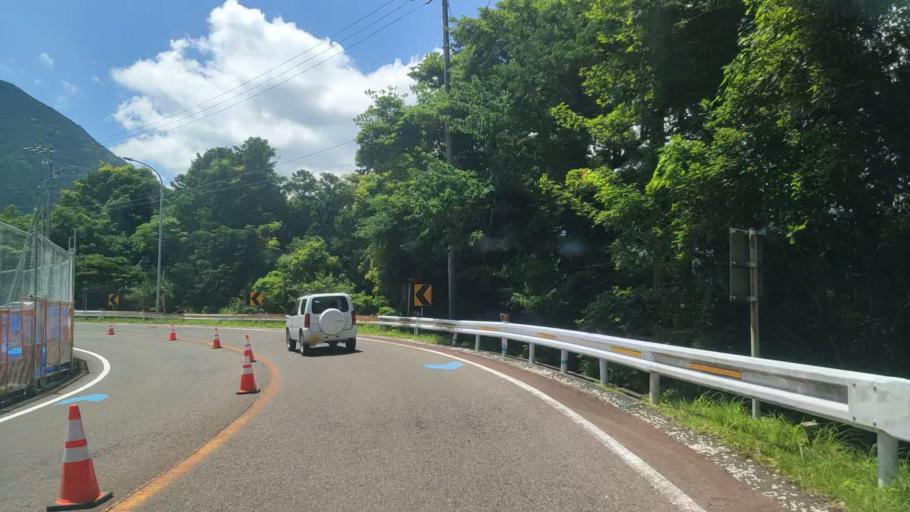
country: JP
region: Mie
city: Owase
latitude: 34.1025
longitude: 136.1993
